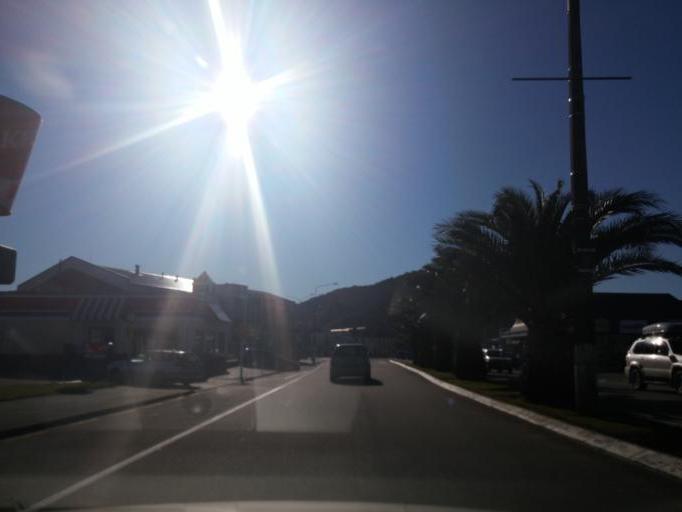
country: NZ
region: West Coast
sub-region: Grey District
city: Greymouth
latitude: -42.4512
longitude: 171.2102
